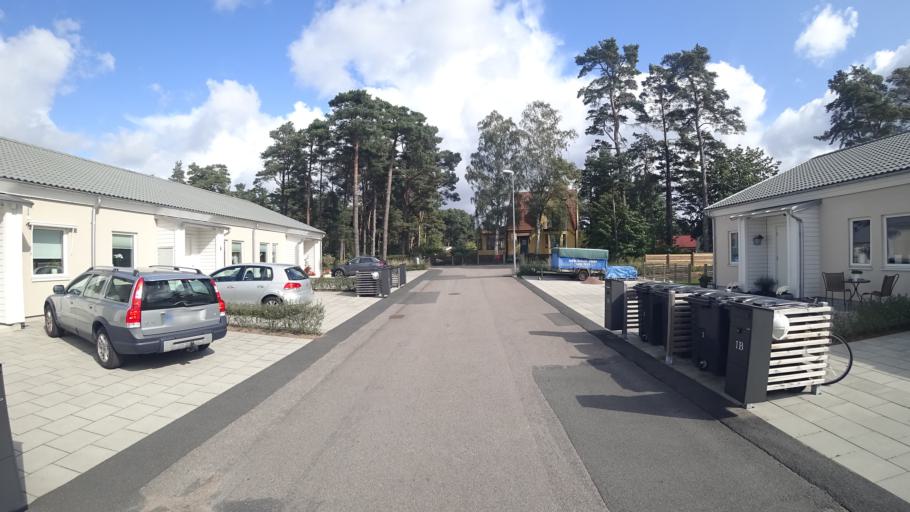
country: SE
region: Skane
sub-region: Kristianstads Kommun
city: Ahus
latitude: 55.9345
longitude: 14.3078
